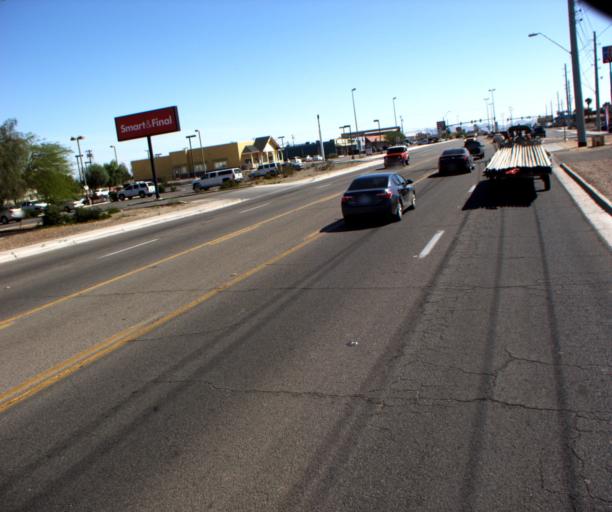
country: US
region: Arizona
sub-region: Yuma County
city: Yuma
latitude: 32.6985
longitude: -114.6192
